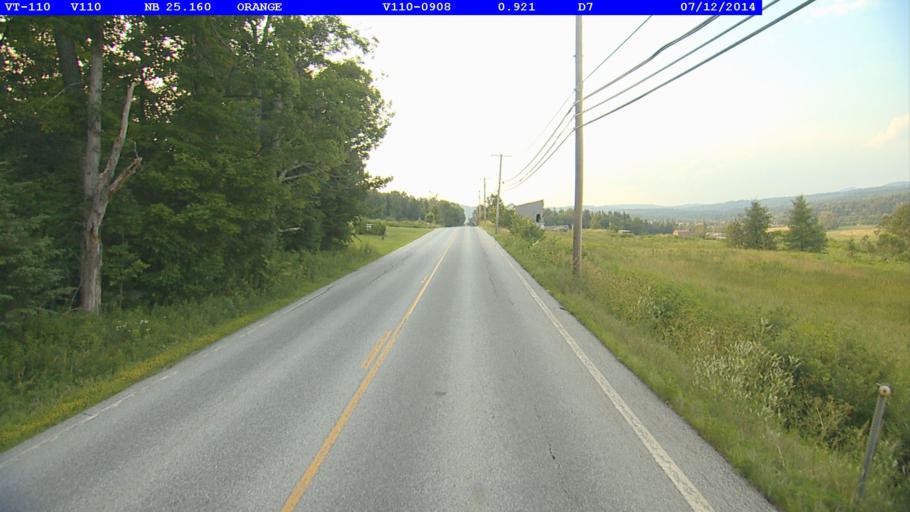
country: US
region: Vermont
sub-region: Washington County
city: South Barre
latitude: 44.1374
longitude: -72.4325
